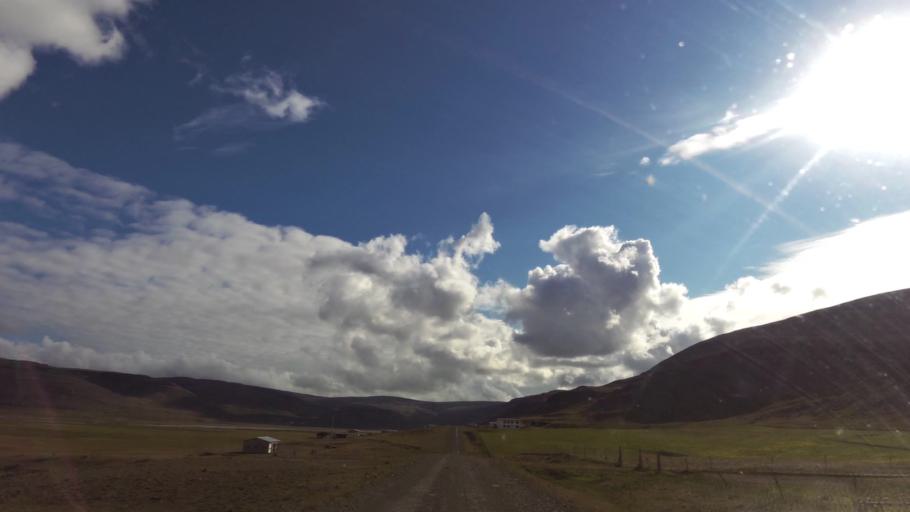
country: IS
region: West
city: Olafsvik
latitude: 65.5863
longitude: -24.1305
